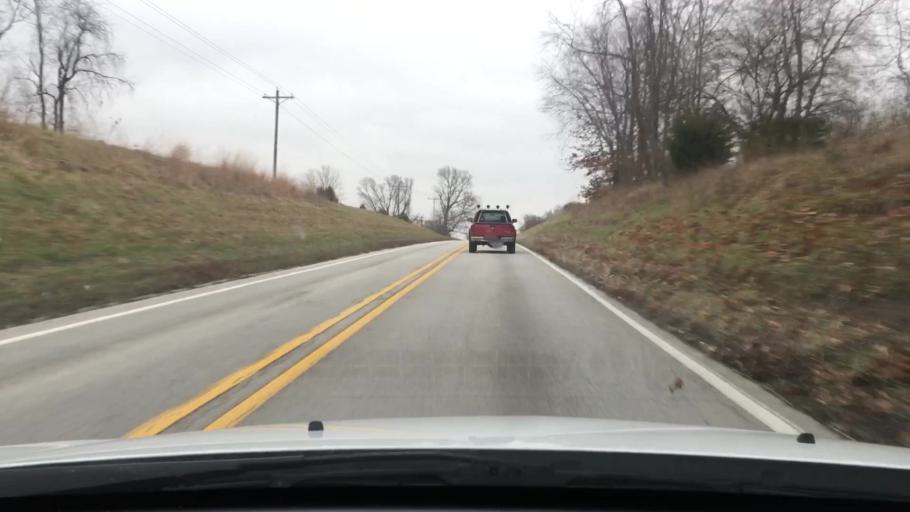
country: US
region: Missouri
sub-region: Pike County
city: Louisiana
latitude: 39.5235
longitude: -90.9413
